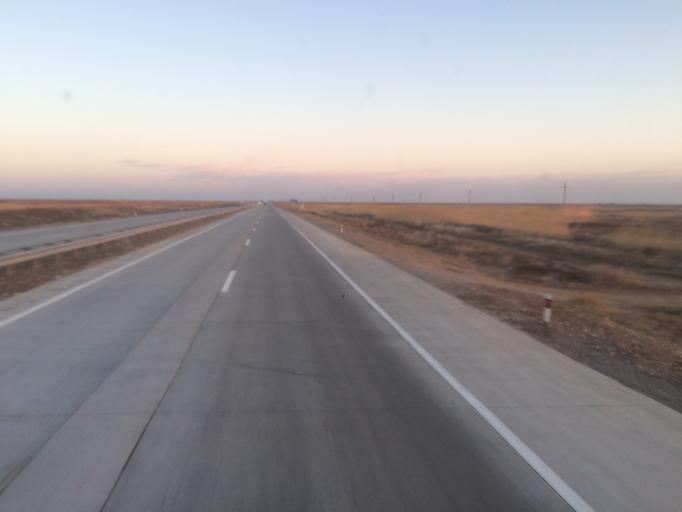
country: KZ
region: Ongtustik Qazaqstan
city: Bayaldyr
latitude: 43.0526
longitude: 68.6970
